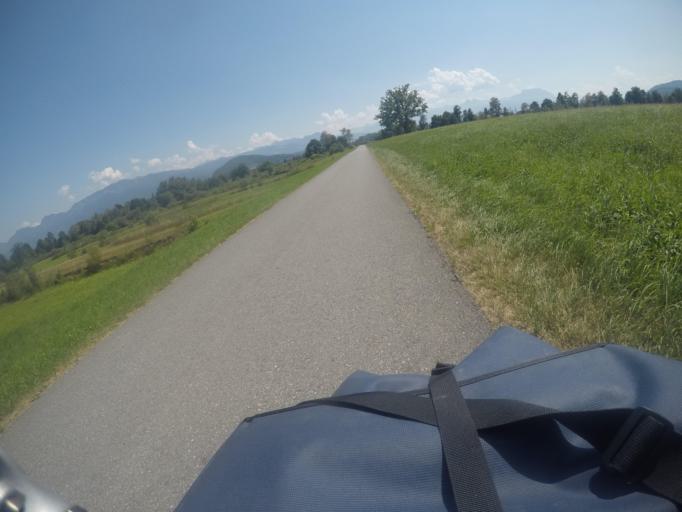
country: CH
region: Saint Gallen
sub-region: Wahlkreis Rheintal
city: Altstatten
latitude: 47.3592
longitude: 9.5711
